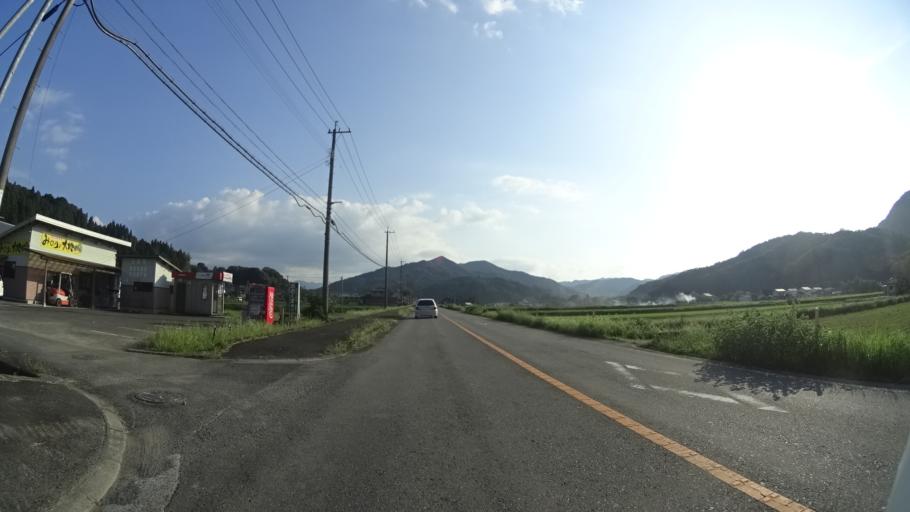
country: JP
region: Oita
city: Bungo-Takada-shi
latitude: 33.4586
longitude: 131.3302
